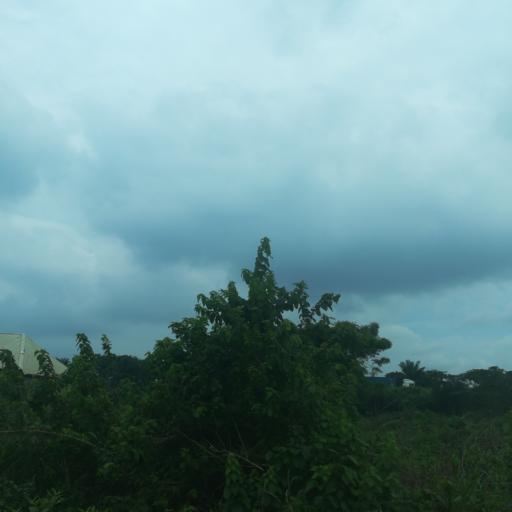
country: NG
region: Lagos
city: Ejirin
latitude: 6.6443
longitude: 3.7276
